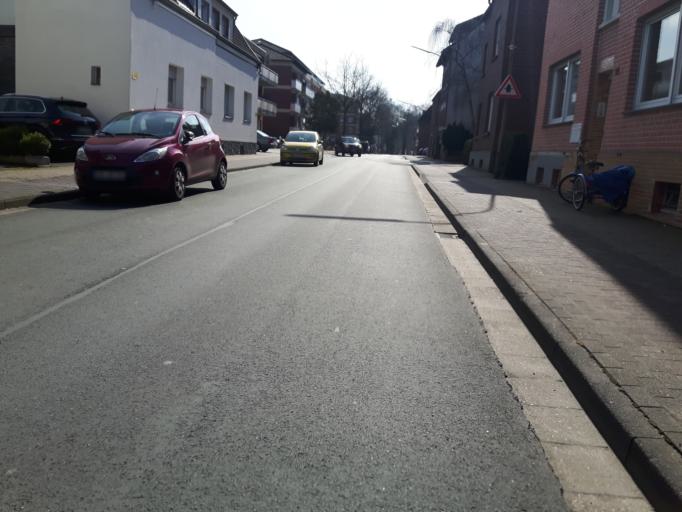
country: DE
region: North Rhine-Westphalia
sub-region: Regierungsbezirk Munster
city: Dulmen
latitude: 51.8300
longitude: 7.2867
